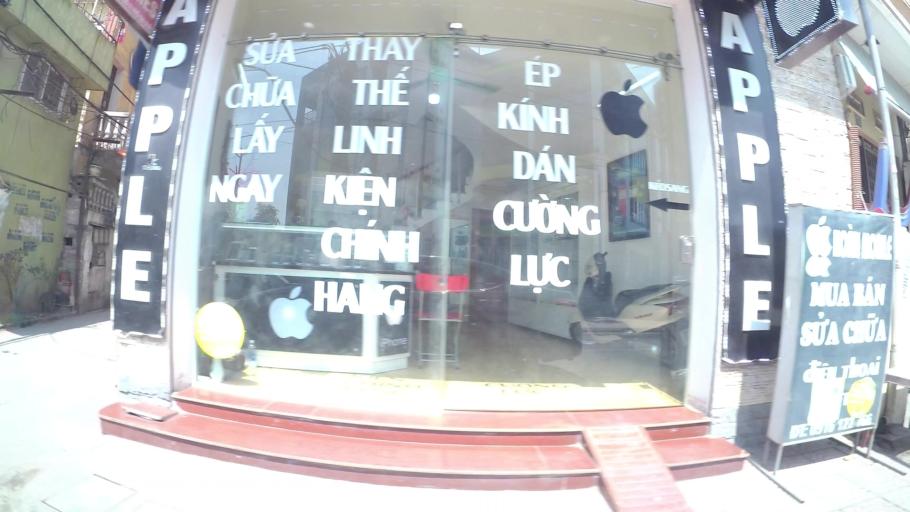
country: VN
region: Ha Noi
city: Hoan Kiem
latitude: 21.0530
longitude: 105.8780
